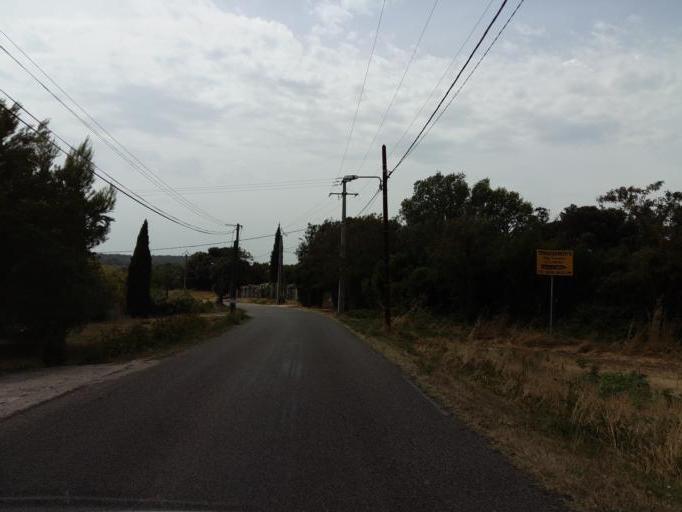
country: FR
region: Provence-Alpes-Cote d'Azur
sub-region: Departement du Vaucluse
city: Piolenc
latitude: 44.1872
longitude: 4.7747
